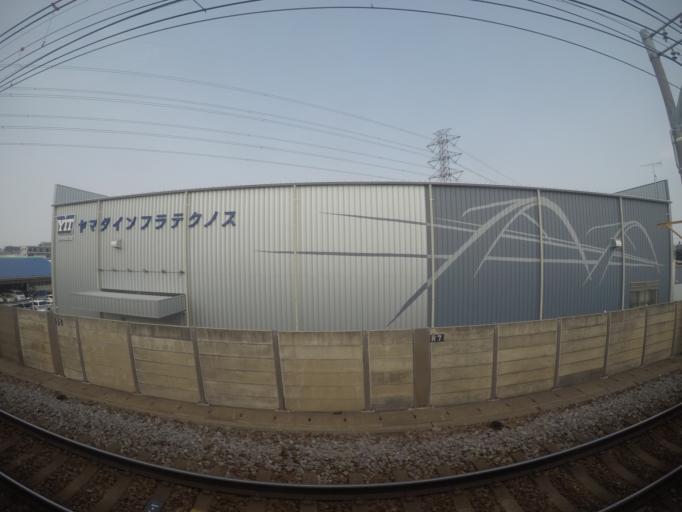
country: JP
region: Aichi
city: Obu
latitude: 35.0638
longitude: 136.9103
